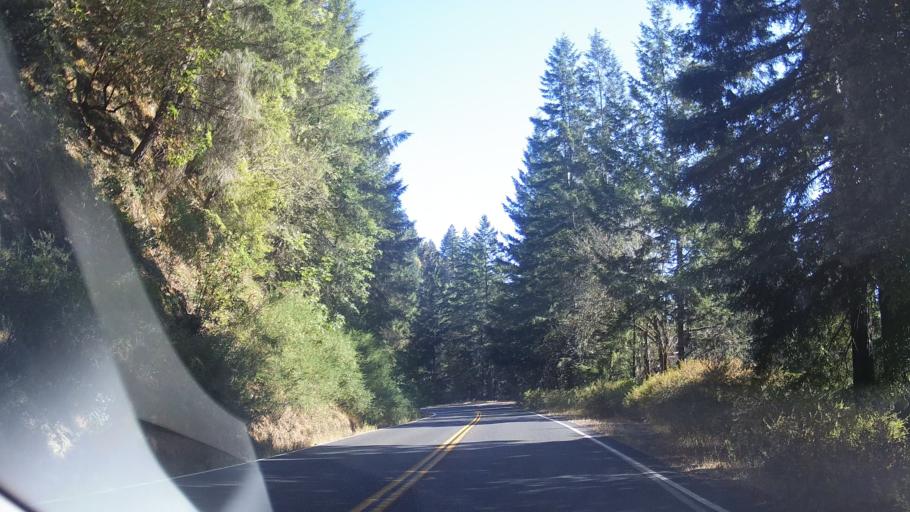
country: US
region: California
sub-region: Mendocino County
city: Brooktrails
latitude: 39.3741
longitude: -123.4952
